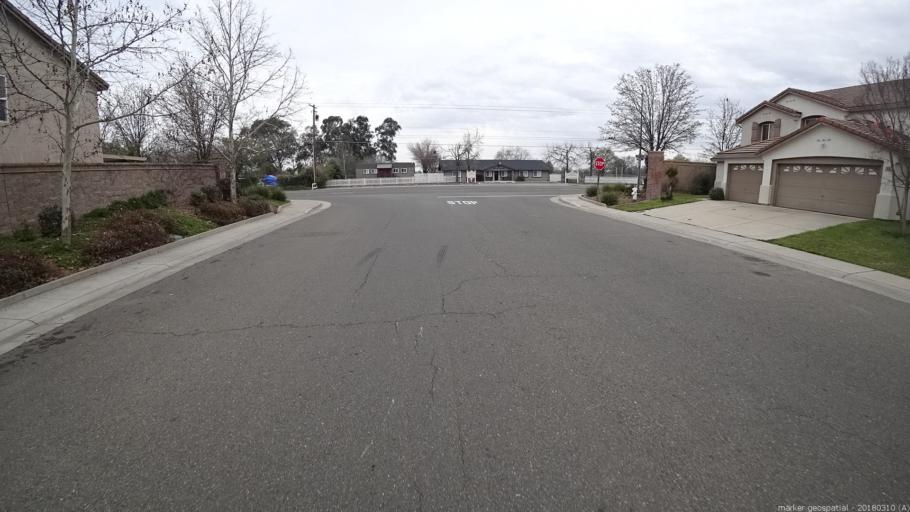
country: US
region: California
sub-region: Sacramento County
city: Vineyard
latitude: 38.4813
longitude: -121.3748
